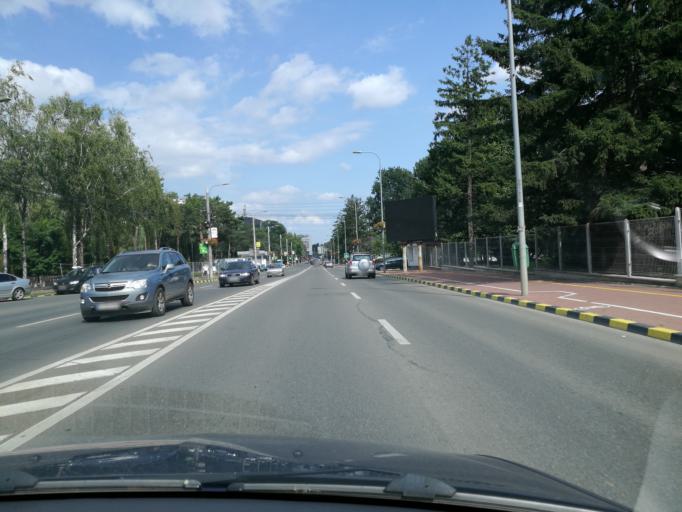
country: RO
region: Suceava
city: Suceava
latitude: 47.6375
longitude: 26.2395
